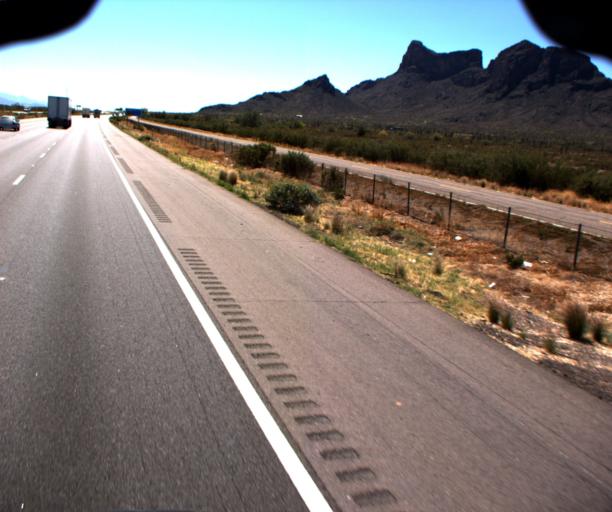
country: US
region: Arizona
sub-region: Pinal County
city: Eloy
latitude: 32.6619
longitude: -111.4132
